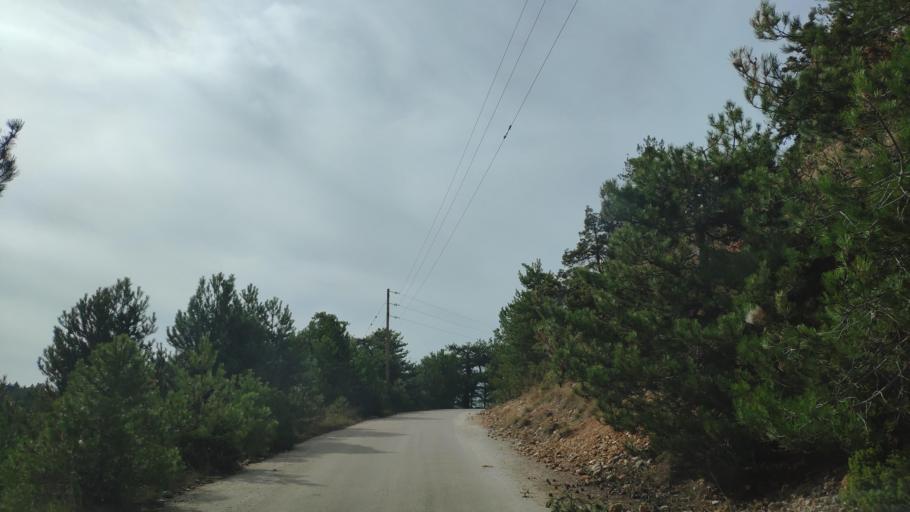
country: GR
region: West Greece
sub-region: Nomos Achaias
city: Aiyira
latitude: 38.0278
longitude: 22.3970
